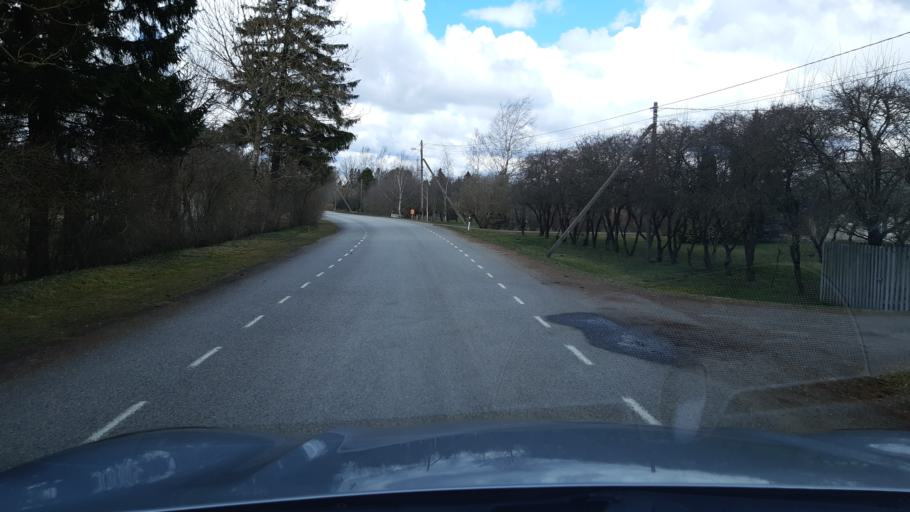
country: EE
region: Raplamaa
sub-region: Kehtna vald
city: Kehtna
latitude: 59.0388
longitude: 25.1298
